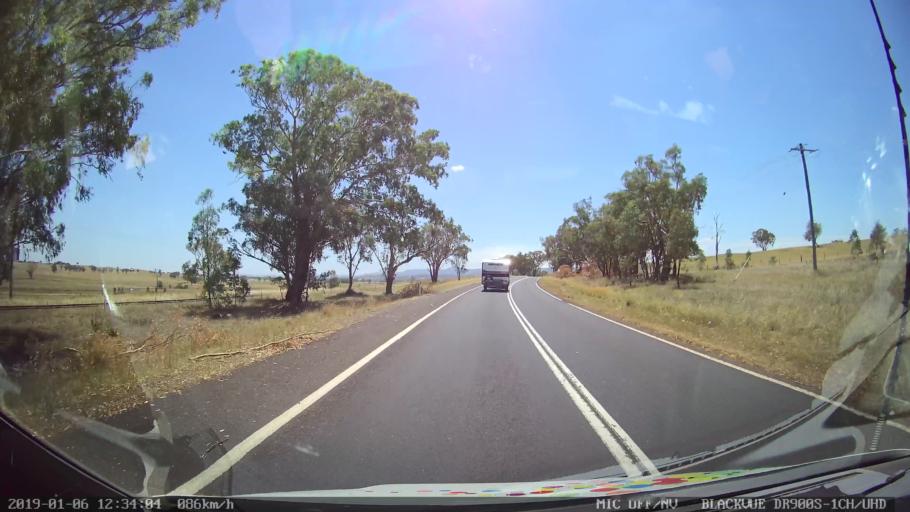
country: AU
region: New South Wales
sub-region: Tamworth Municipality
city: Phillip
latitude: -31.1328
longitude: 150.8809
